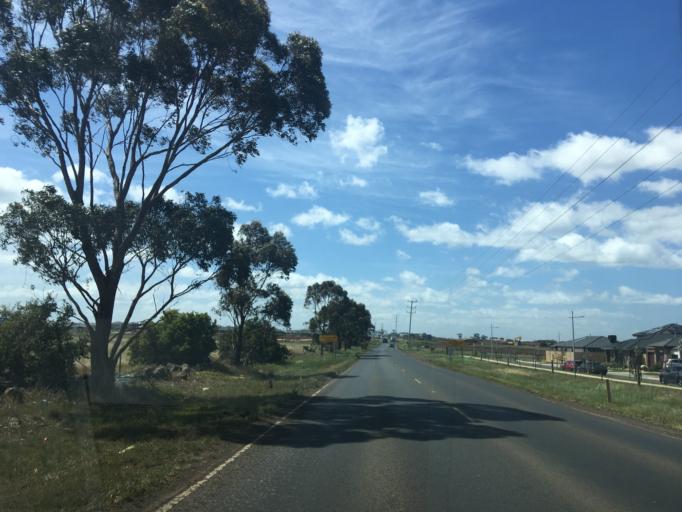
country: AU
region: Victoria
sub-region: Wyndham
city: Truganina
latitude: -37.8208
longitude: 144.7019
